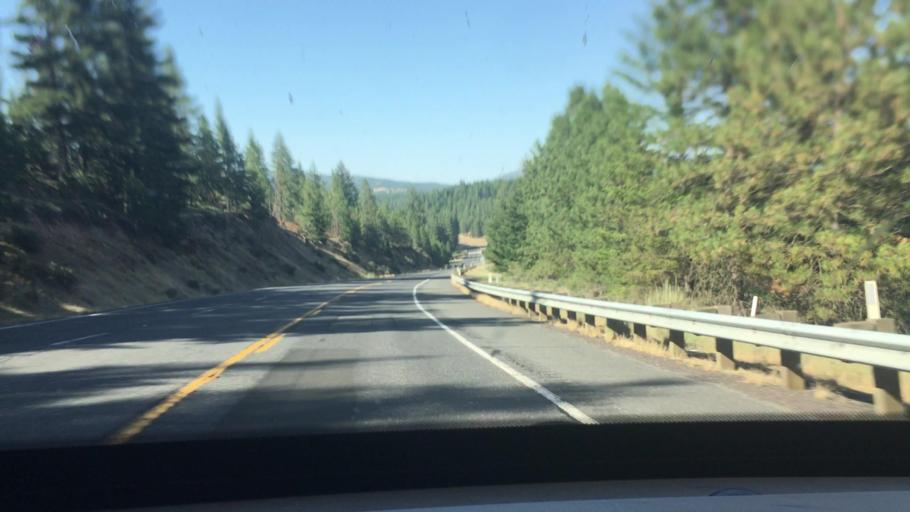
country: US
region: Washington
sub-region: Klickitat County
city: Goldendale
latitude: 45.9079
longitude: -120.7114
